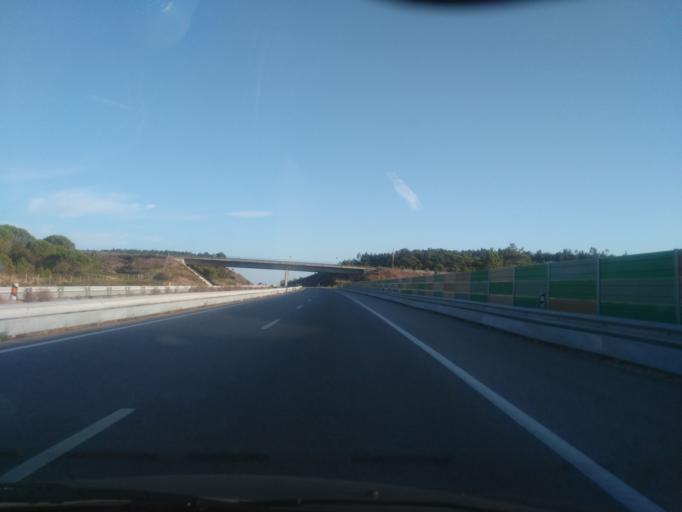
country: PT
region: Coimbra
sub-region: Figueira da Foz
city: Alhadas
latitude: 40.1928
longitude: -8.8136
